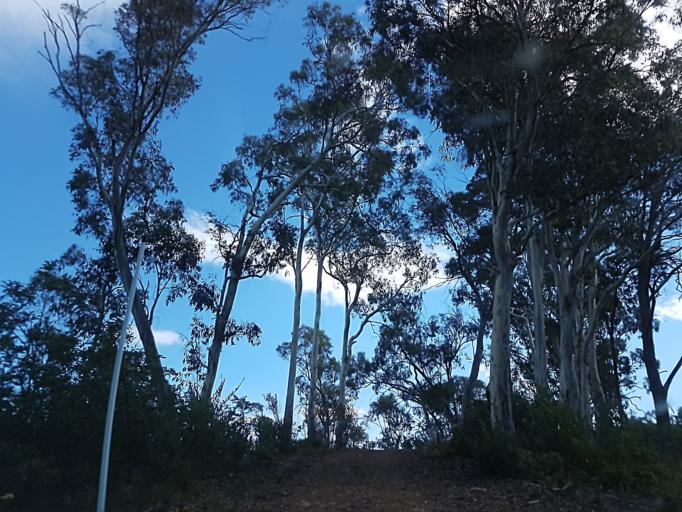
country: AU
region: Victoria
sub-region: Alpine
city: Mount Beauty
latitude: -36.9109
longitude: 147.0156
